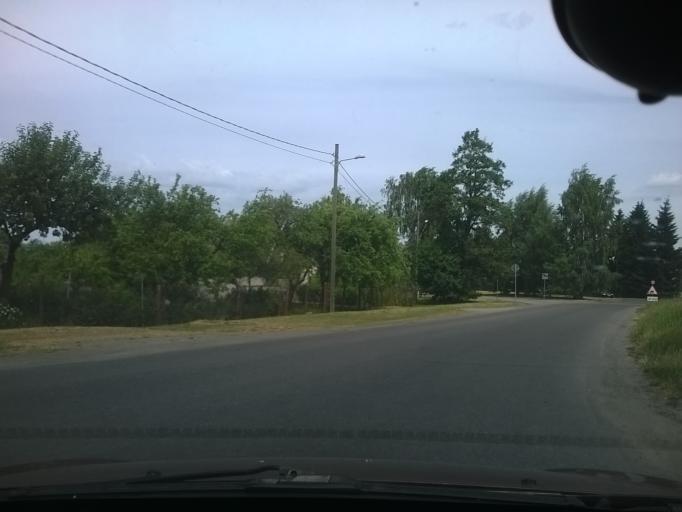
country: EE
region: Harju
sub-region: Tallinna linn
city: Tallinn
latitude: 59.4251
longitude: 24.6892
